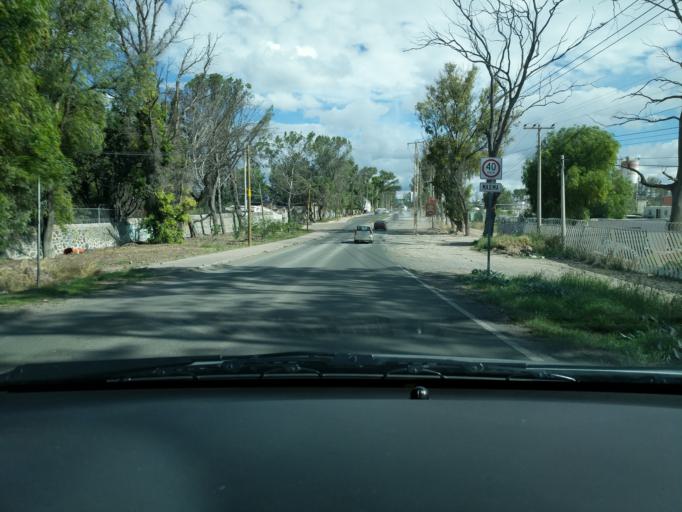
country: MX
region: Queretaro
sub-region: El Marques
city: Hacienda la Cruz [Fraccionamiento]
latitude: 20.6246
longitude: -100.2605
